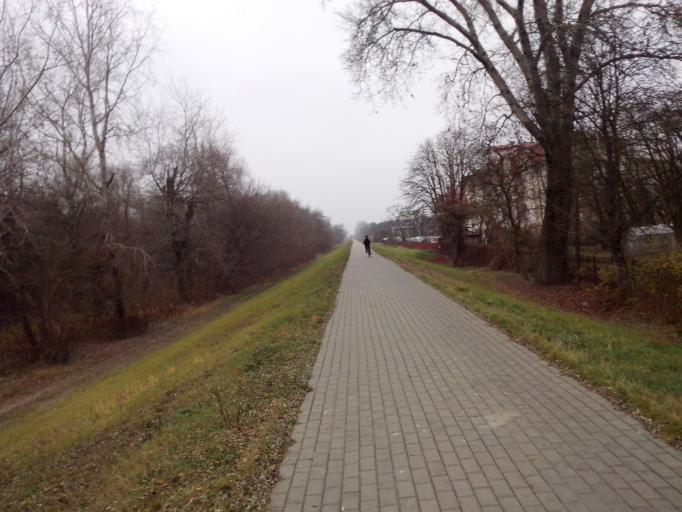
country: PL
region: Masovian Voivodeship
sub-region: Warszawa
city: Bielany
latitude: 52.3295
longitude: 20.9336
